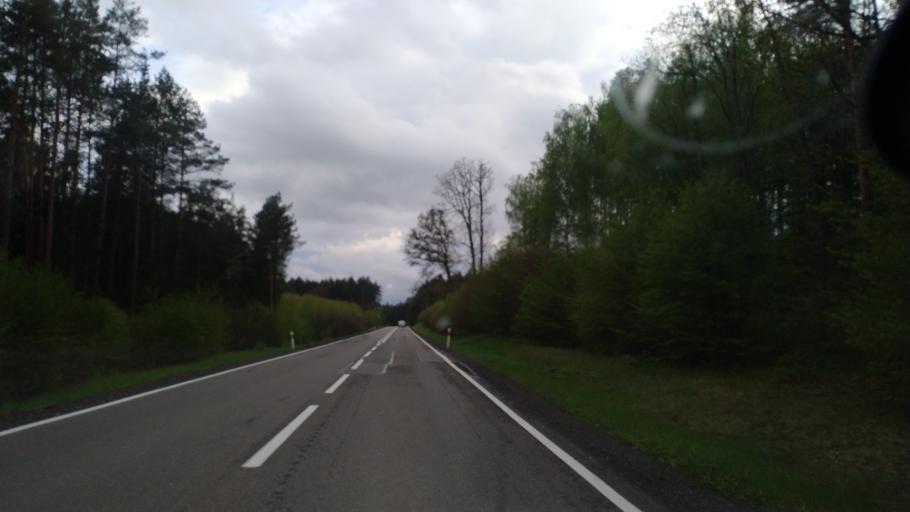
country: PL
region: Pomeranian Voivodeship
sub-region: Powiat kwidzynski
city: Ryjewo
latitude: 53.8244
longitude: 18.9862
